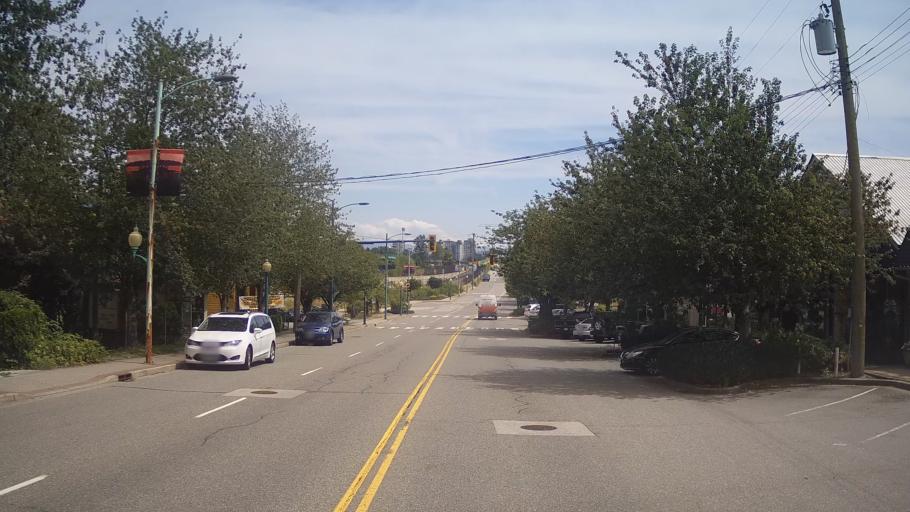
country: CA
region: British Columbia
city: Port Moody
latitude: 49.2776
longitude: -122.8610
